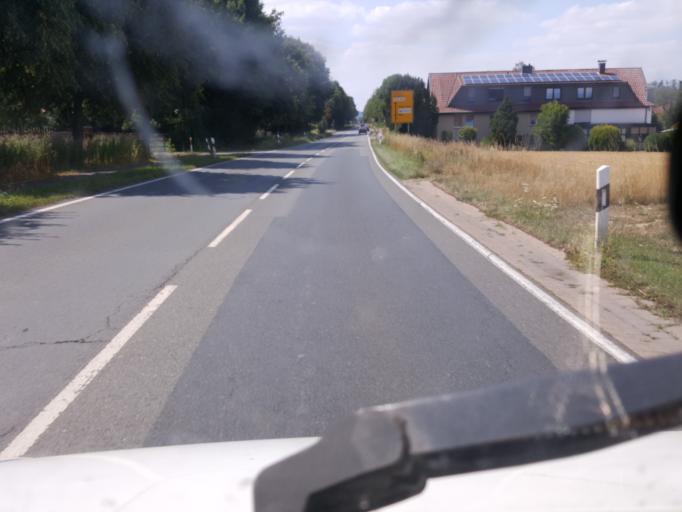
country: DE
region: North Rhine-Westphalia
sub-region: Regierungsbezirk Detmold
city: Minden
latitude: 52.2627
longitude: 8.8528
